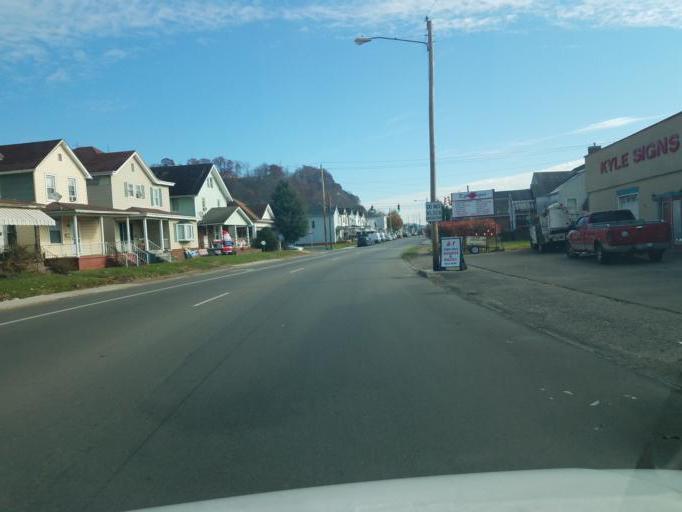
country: US
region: Ohio
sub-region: Scioto County
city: New Boston
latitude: 38.7544
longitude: -82.9318
